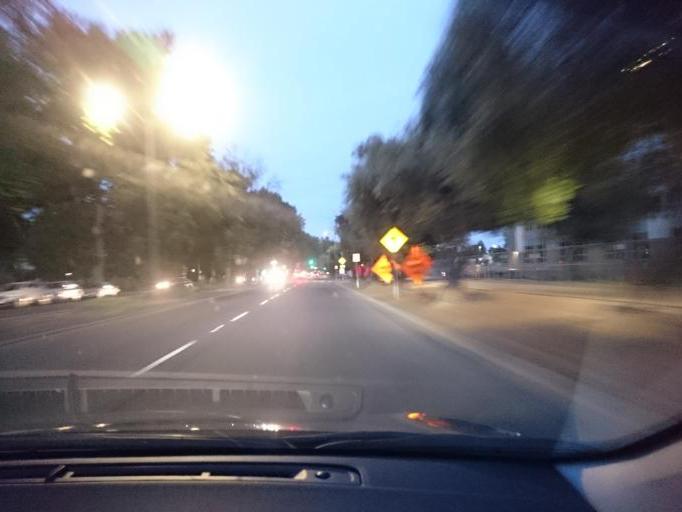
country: US
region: California
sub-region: Yolo County
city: Davis
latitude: 38.5462
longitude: -121.7551
